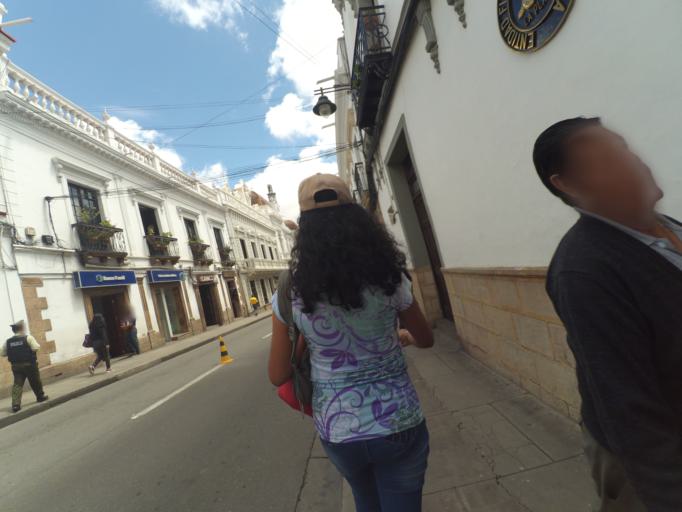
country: BO
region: Chuquisaca
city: Sucre
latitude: -19.0477
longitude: -65.2586
